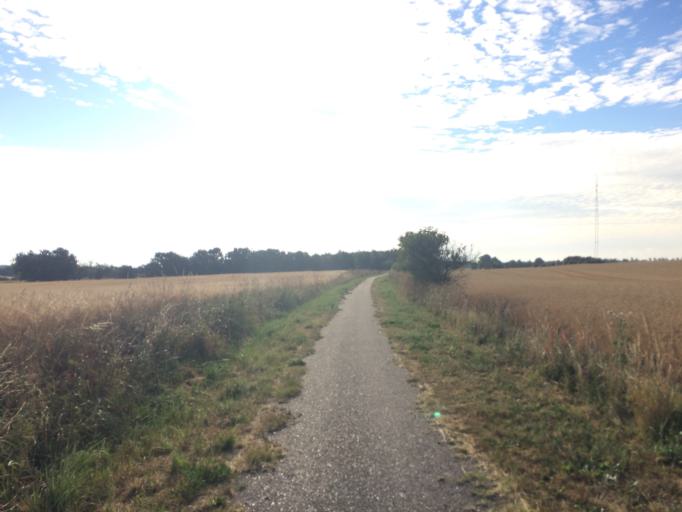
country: DK
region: Central Jutland
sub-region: Skive Kommune
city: Skive
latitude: 56.5999
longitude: 8.9881
